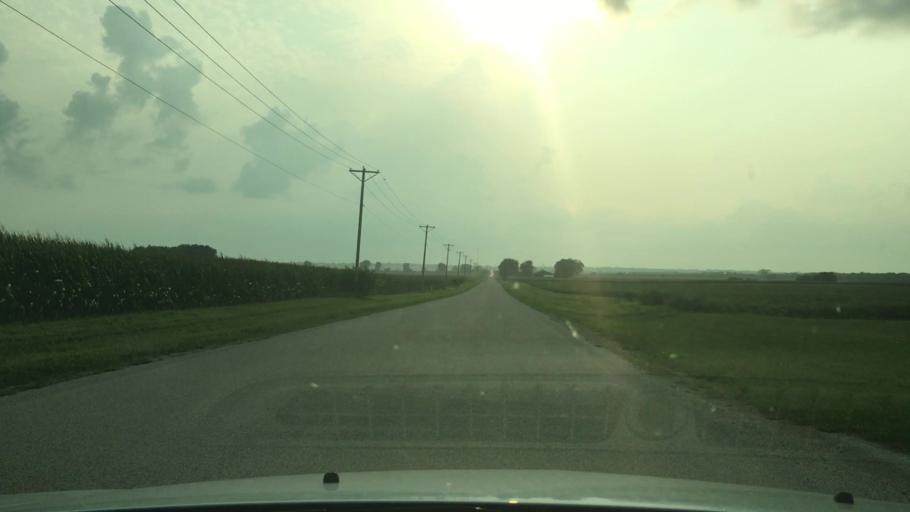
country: US
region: Illinois
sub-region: Ogle County
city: Rochelle
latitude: 41.9203
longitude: -89.0042
